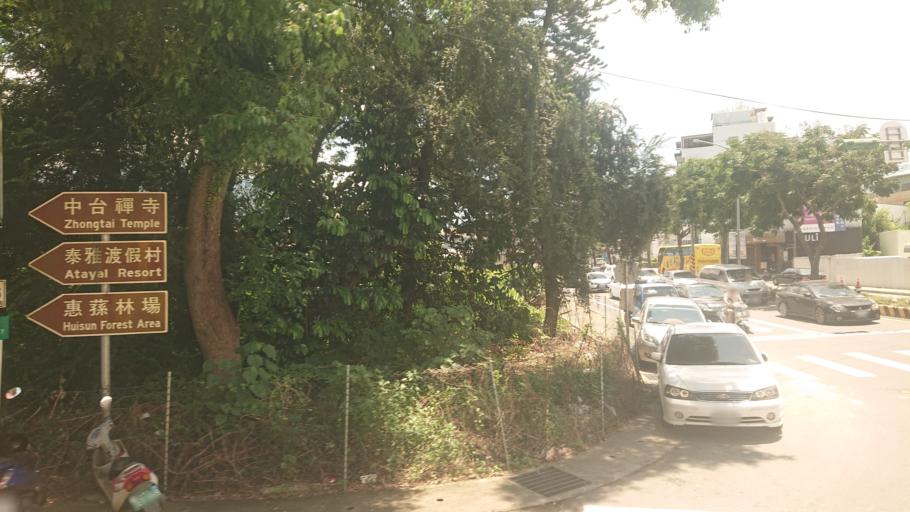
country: TW
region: Taiwan
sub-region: Nantou
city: Puli
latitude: 23.9730
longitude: 120.9630
